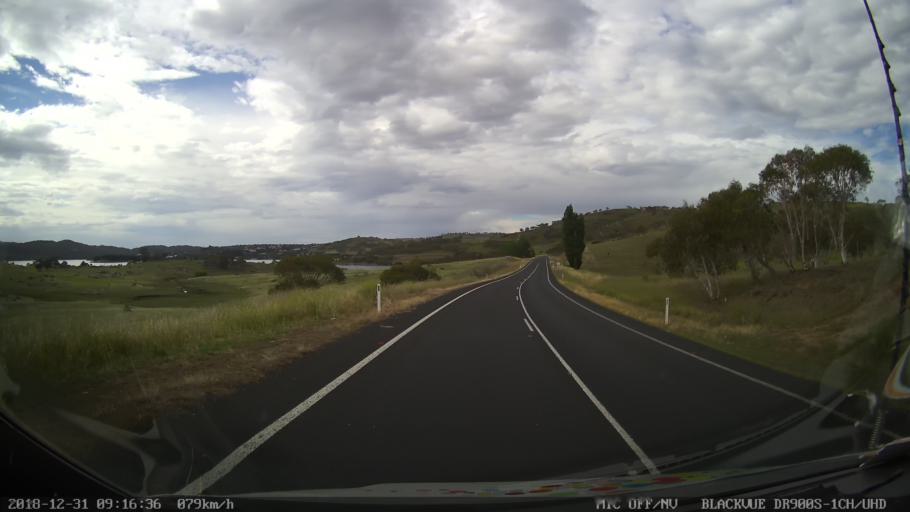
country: AU
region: New South Wales
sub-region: Snowy River
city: Jindabyne
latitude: -36.3977
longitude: 148.5971
